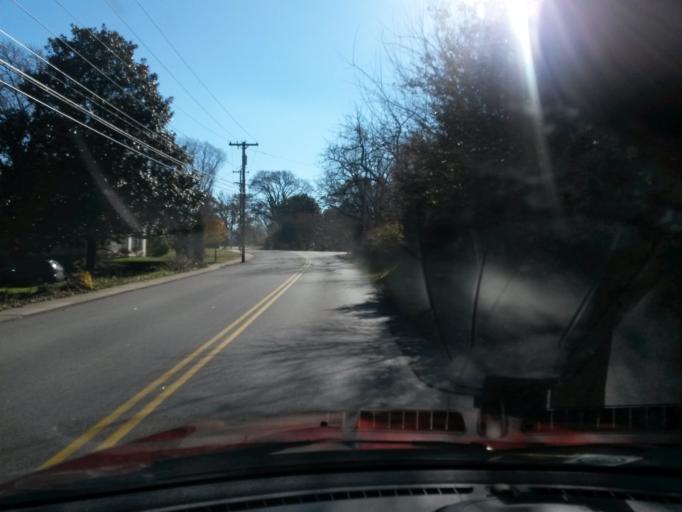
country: US
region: Virginia
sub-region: City of Bedford
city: Bedford
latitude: 37.3411
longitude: -79.5256
